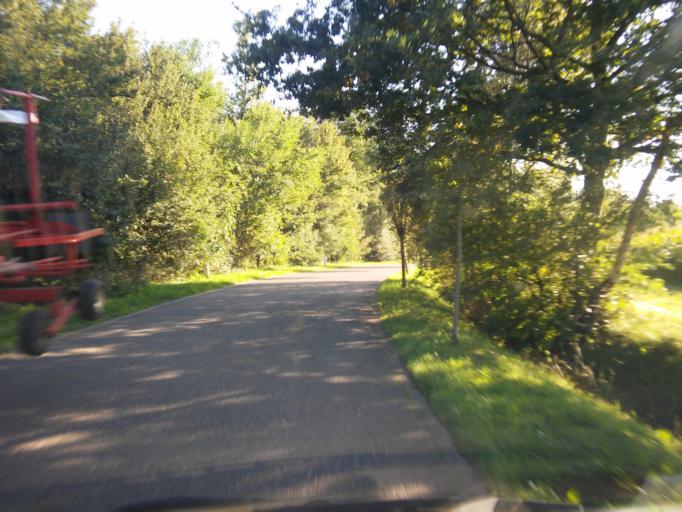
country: BE
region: Flanders
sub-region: Provincie Antwerpen
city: Rumst
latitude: 51.1040
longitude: 4.4334
